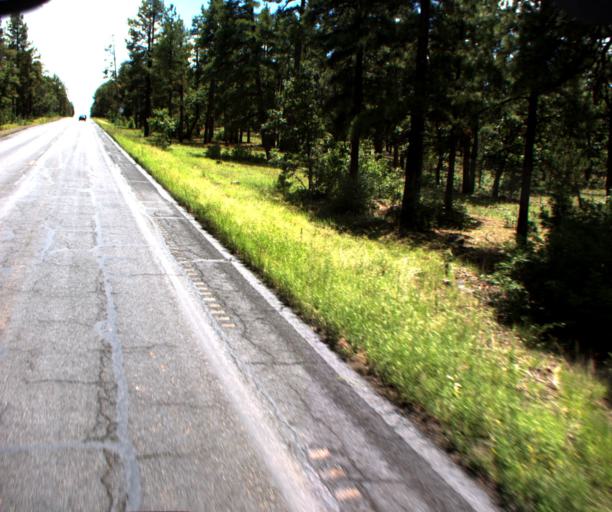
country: US
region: Arizona
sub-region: Gila County
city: Pine
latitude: 34.4935
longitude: -111.4584
